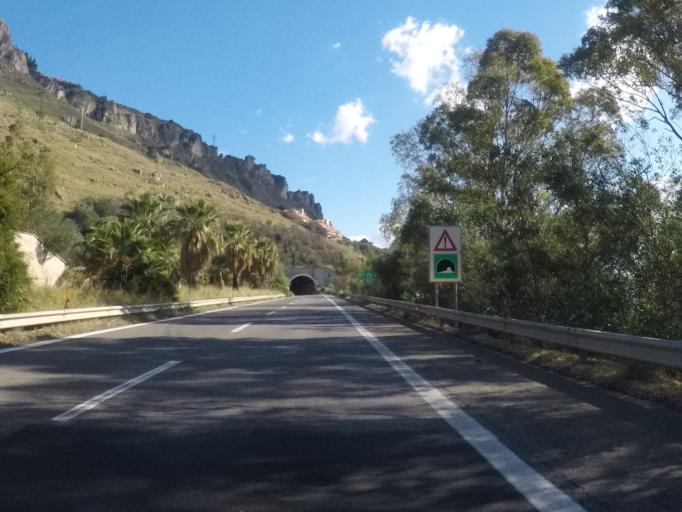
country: IT
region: Sicily
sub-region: Messina
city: Forza d'Agro
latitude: 37.9074
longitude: 15.3350
